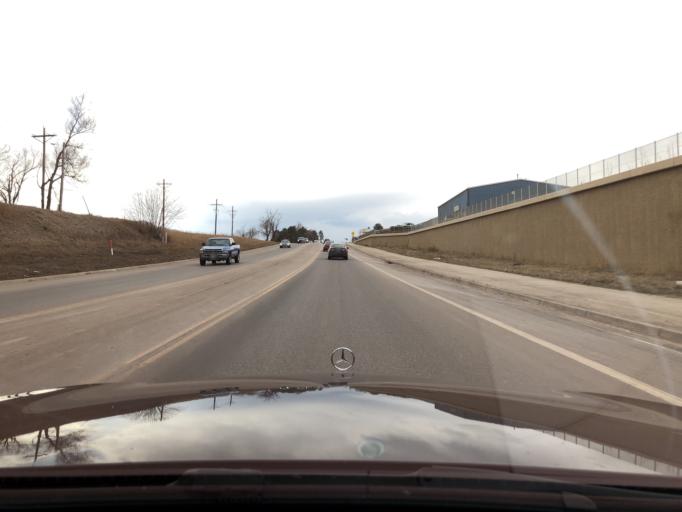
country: US
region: Colorado
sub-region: Boulder County
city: Gunbarrel
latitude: 40.0148
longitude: -105.1839
